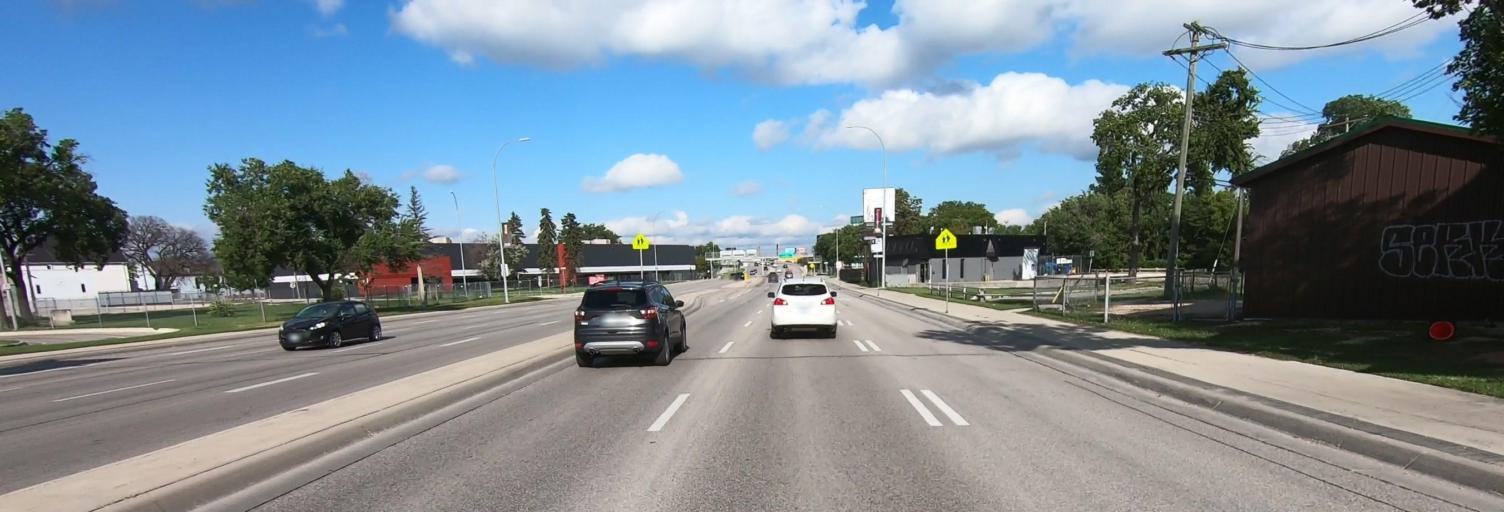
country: CA
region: Manitoba
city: Winnipeg
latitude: 49.9019
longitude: -97.1329
